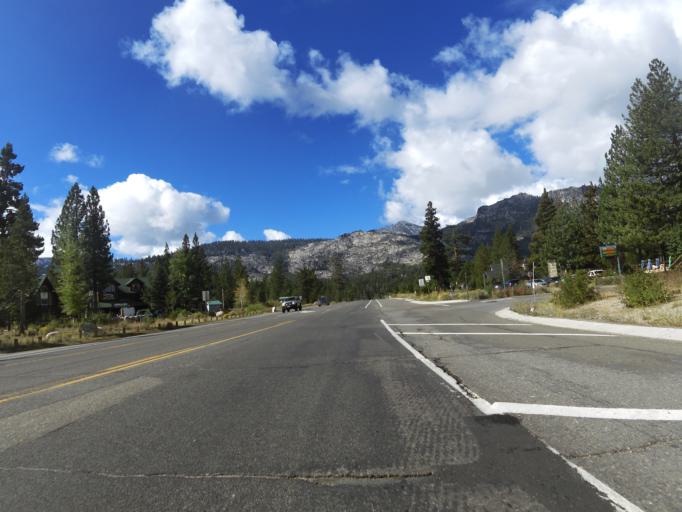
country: US
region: California
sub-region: El Dorado County
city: South Lake Tahoe
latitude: 38.8530
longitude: -120.0183
